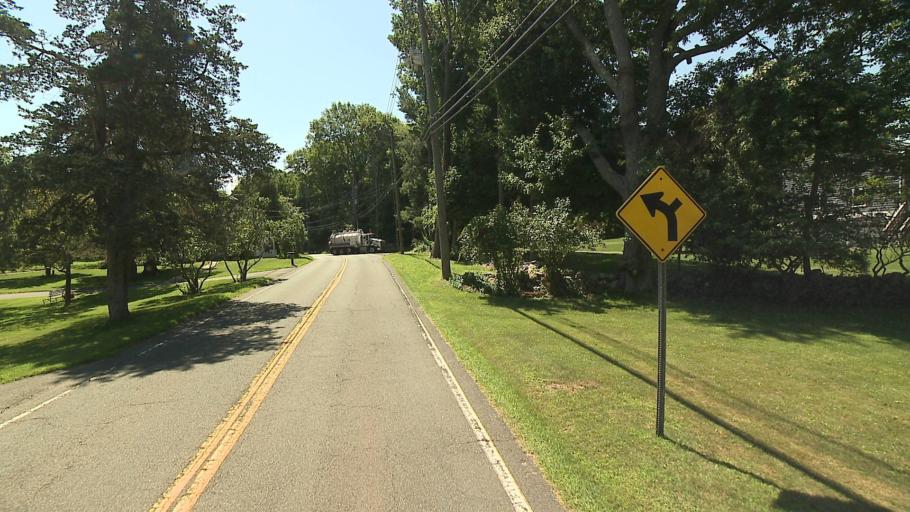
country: US
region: Connecticut
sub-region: Fairfield County
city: Ridgefield
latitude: 41.2837
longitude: -73.5150
